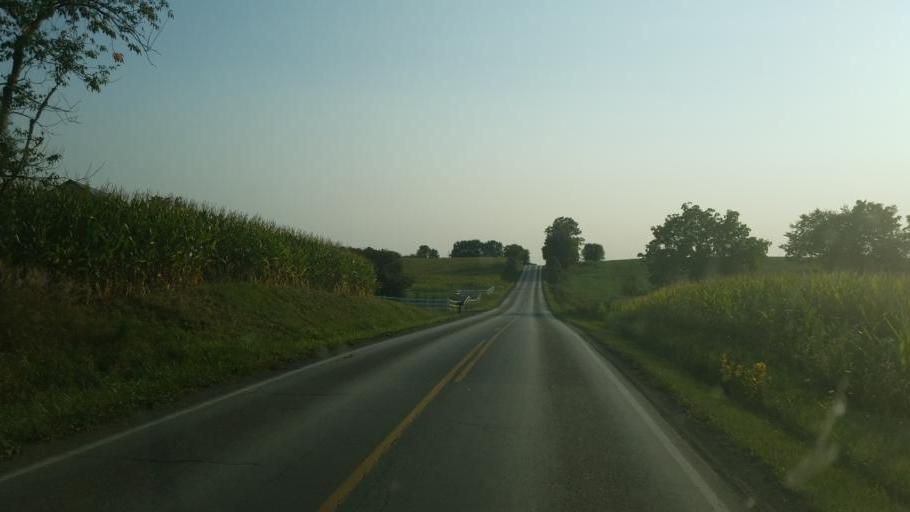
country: US
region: Ohio
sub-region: Wayne County
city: Apple Creek
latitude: 40.7523
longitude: -81.8010
